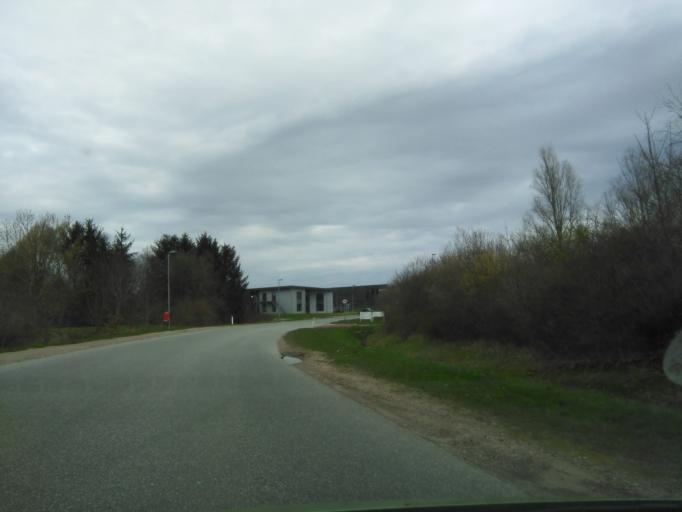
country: DK
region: Central Jutland
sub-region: Skanderborg Kommune
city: Stilling
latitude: 56.0644
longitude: 9.9799
